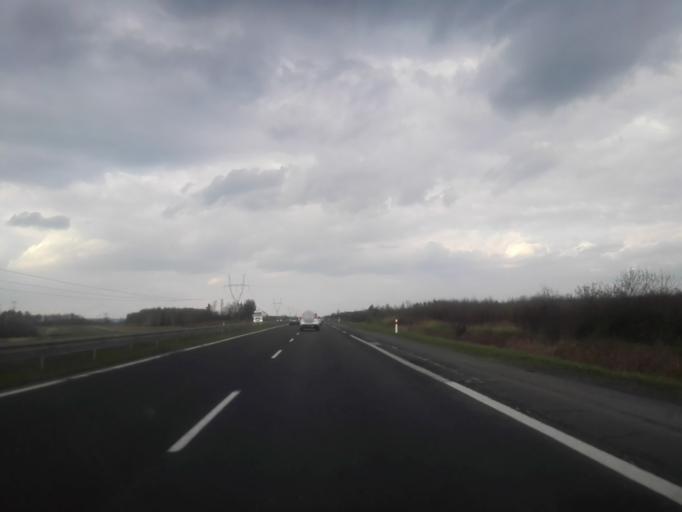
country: PL
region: Lodz Voivodeship
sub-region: Powiat radomszczanski
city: Radomsko
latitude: 51.1176
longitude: 19.4002
